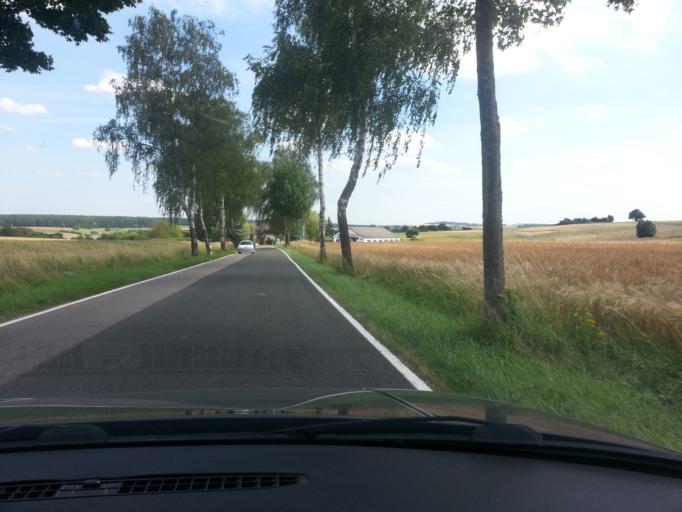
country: DE
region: Rheinland-Pfalz
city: Hornbach
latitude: 49.1764
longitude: 7.3013
